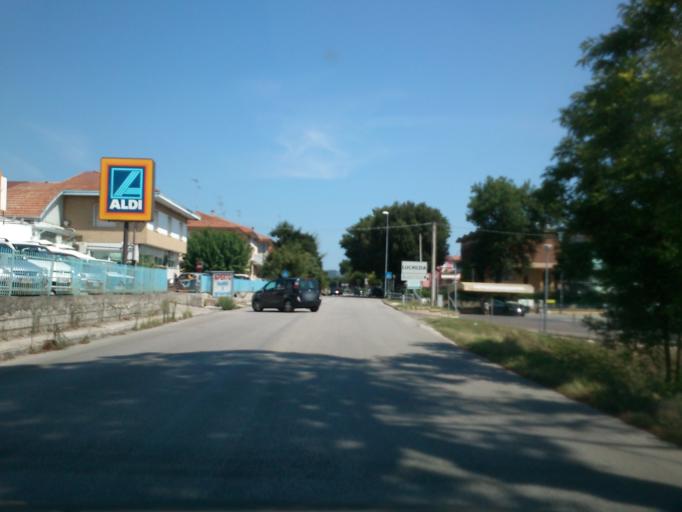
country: IT
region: The Marches
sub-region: Provincia di Pesaro e Urbino
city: Lucrezia
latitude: 43.7686
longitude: 12.9316
